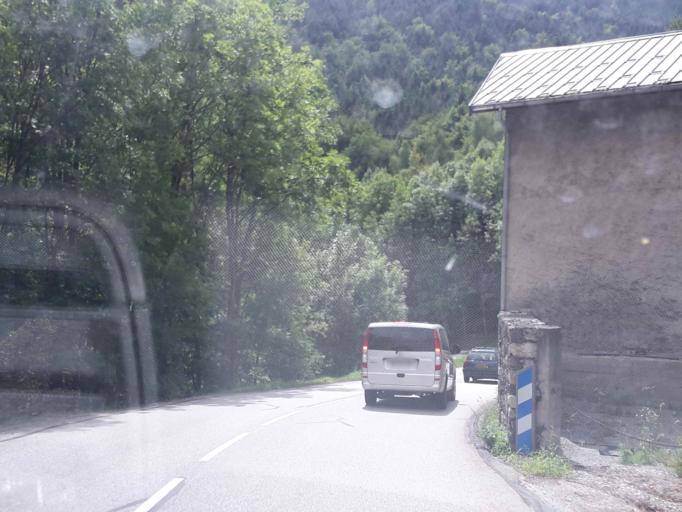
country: FR
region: Rhone-Alpes
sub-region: Departement de la Savoie
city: Saint-Michel-de-Maurienne
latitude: 45.2086
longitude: 6.4579
